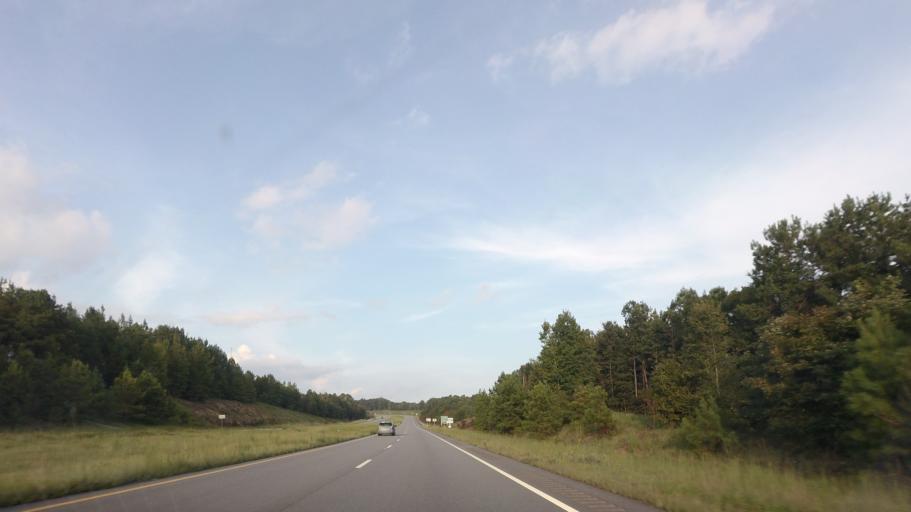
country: US
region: Georgia
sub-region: Wilkinson County
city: Gordon
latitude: 32.8562
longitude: -83.3865
